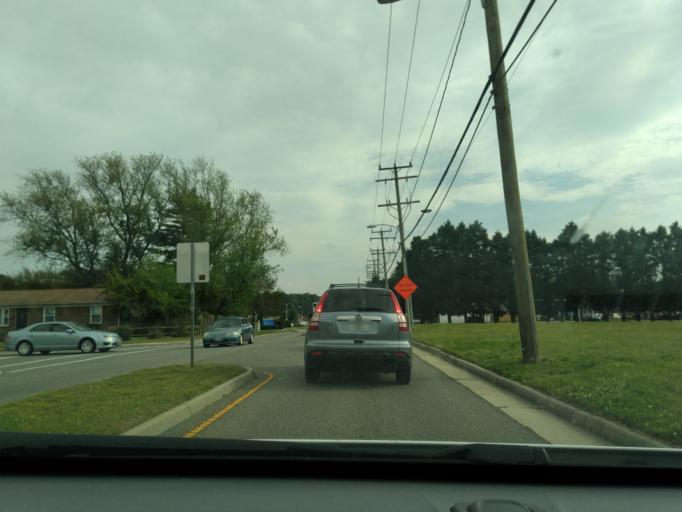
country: US
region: Virginia
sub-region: York County
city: Yorktown
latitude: 37.1513
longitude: -76.5277
